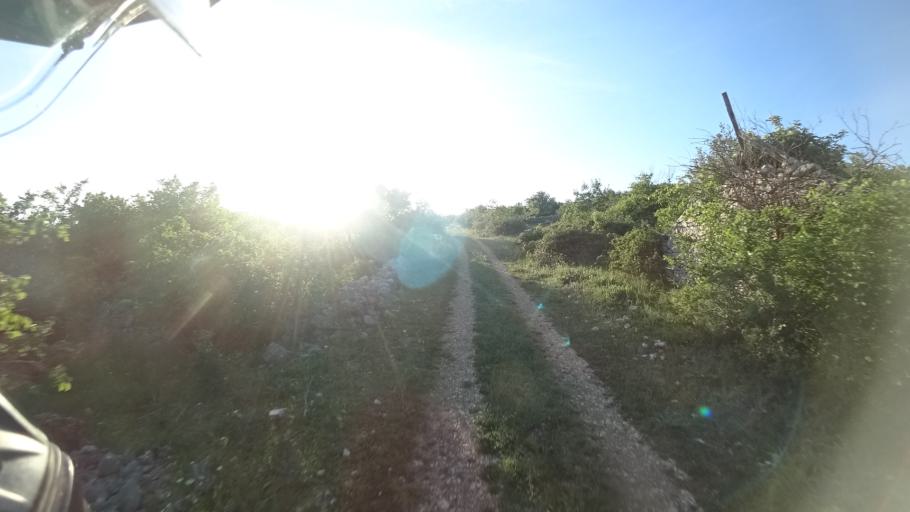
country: HR
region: Sibensko-Kniniska
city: Drnis
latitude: 43.8478
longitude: 16.3443
